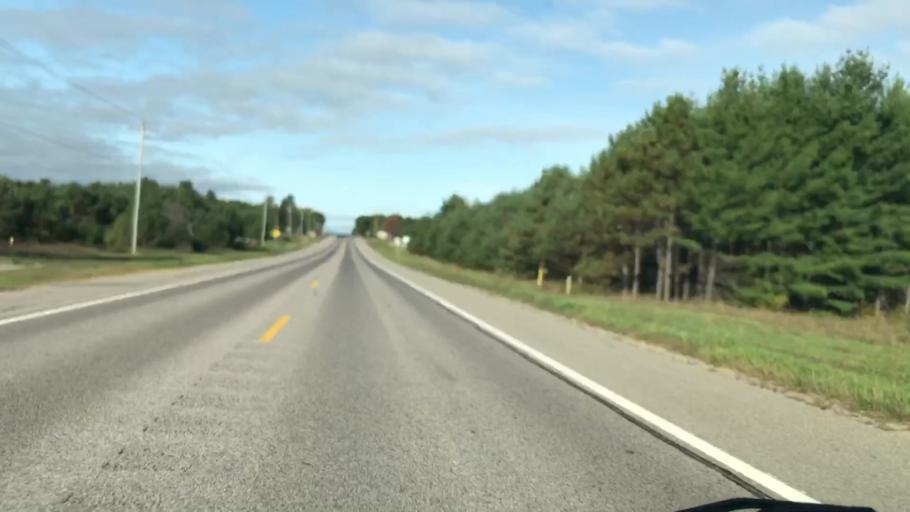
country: US
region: Michigan
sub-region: Luce County
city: Newberry
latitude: 46.3035
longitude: -85.4934
